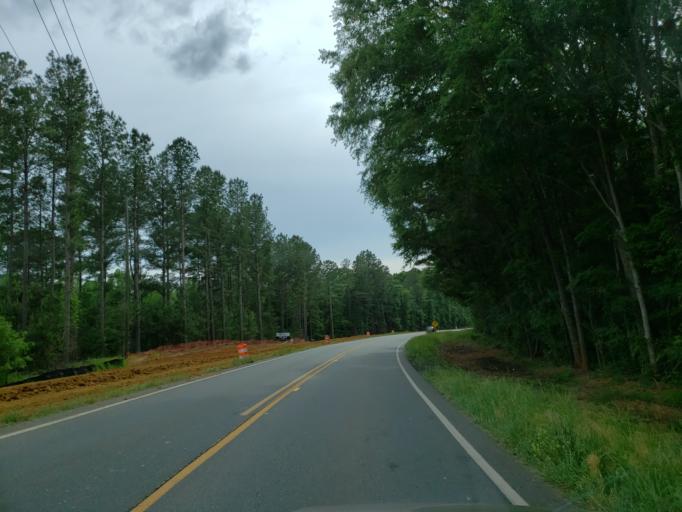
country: US
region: Georgia
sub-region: Macon County
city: Marshallville
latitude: 32.3801
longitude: -83.8819
